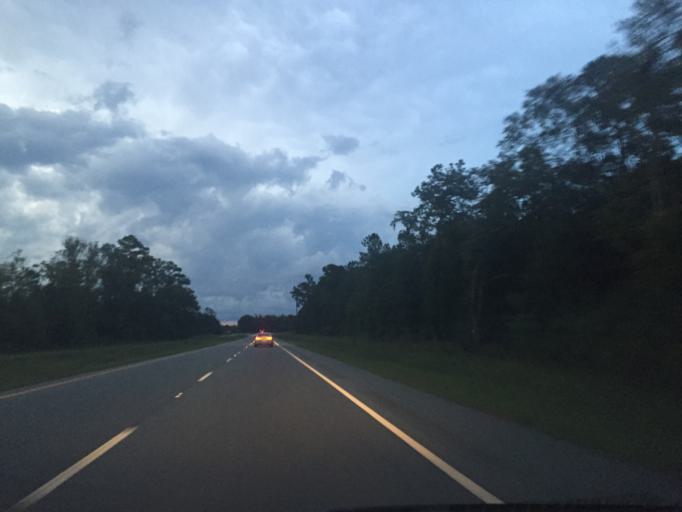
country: US
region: Georgia
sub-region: Liberty County
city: Midway
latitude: 31.8526
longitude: -81.4549
